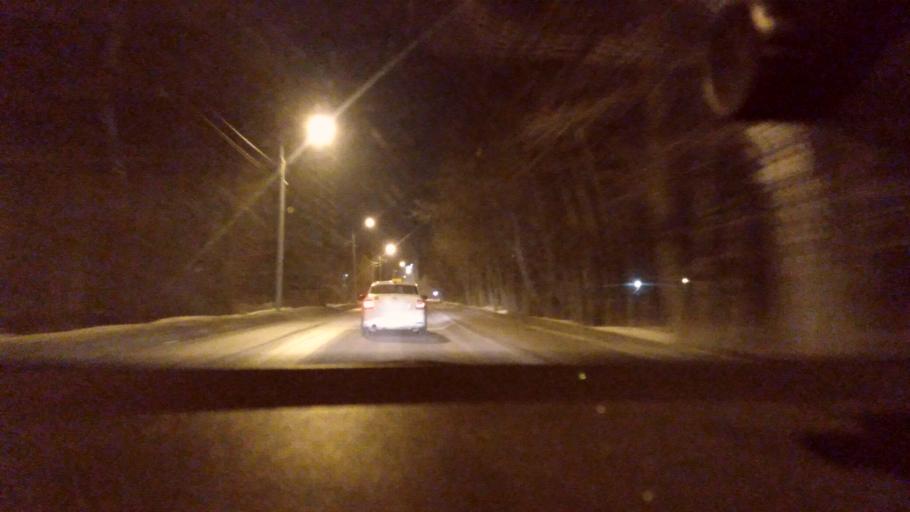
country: RU
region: Moskovskaya
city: Zheleznodorozhnyy
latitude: 55.7411
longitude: 38.0402
